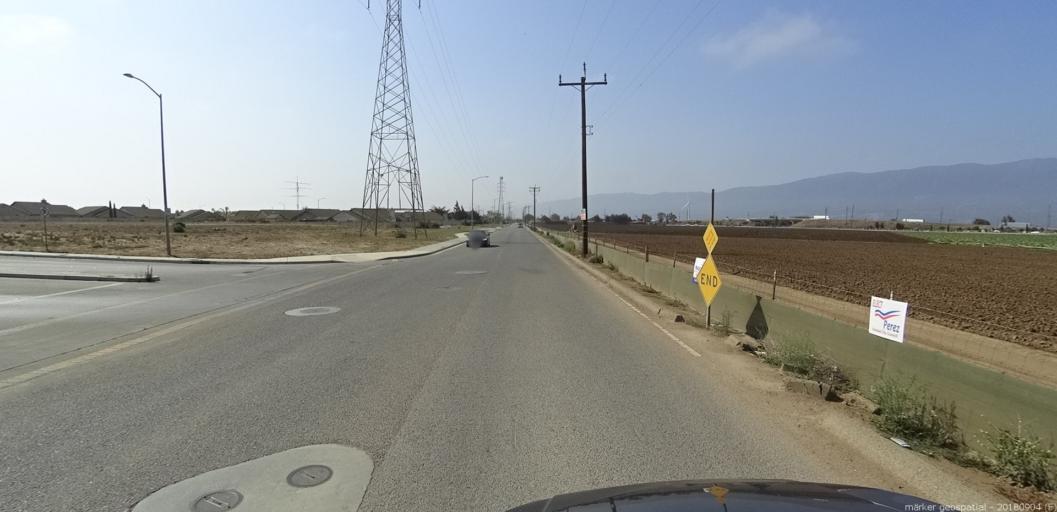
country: US
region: California
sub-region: Monterey County
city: Soledad
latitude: 36.4367
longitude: -121.3337
